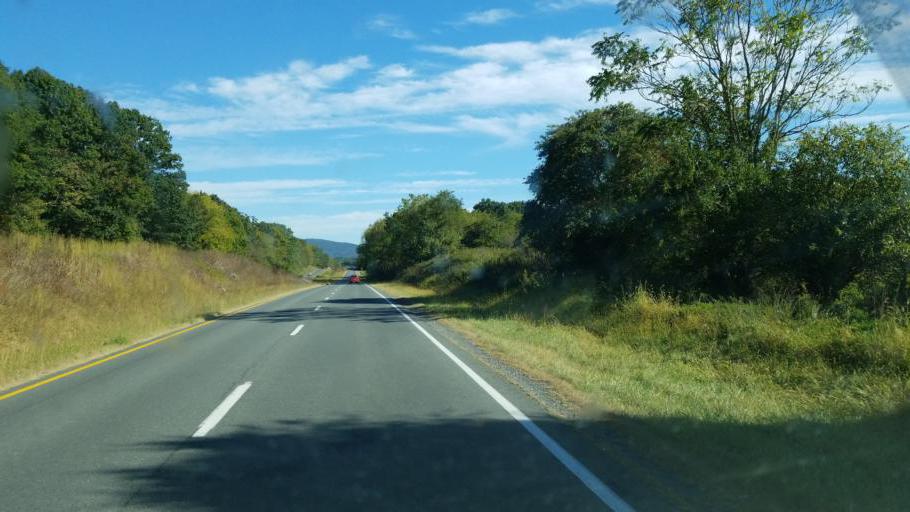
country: US
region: Virginia
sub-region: Warren County
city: Shenandoah Farms
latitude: 39.0651
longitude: -78.0534
